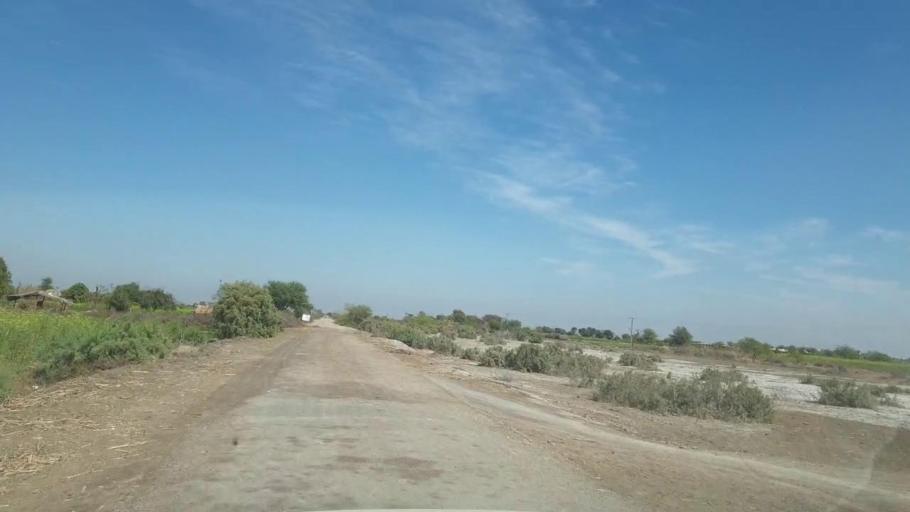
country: PK
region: Sindh
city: Pithoro
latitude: 25.6302
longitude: 69.2173
